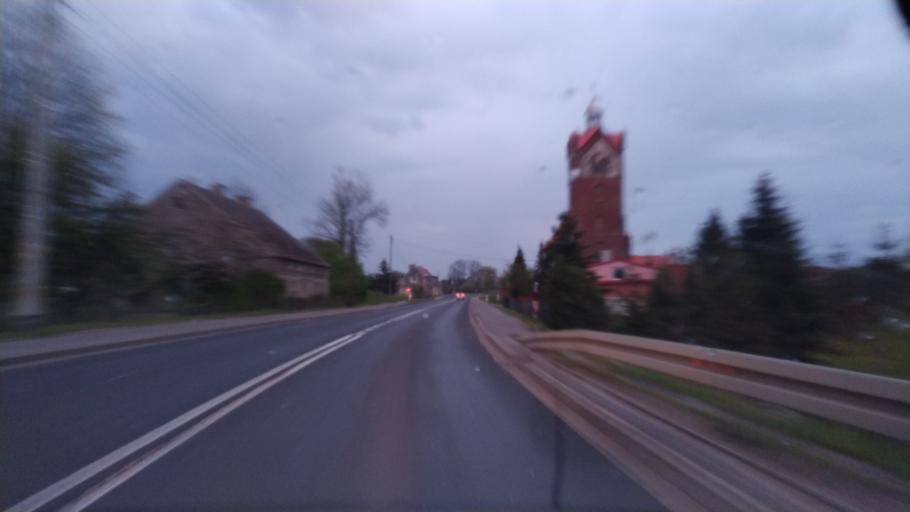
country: PL
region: Greater Poland Voivodeship
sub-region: Powiat pilski
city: Szydlowo
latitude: 53.2479
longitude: 16.5749
